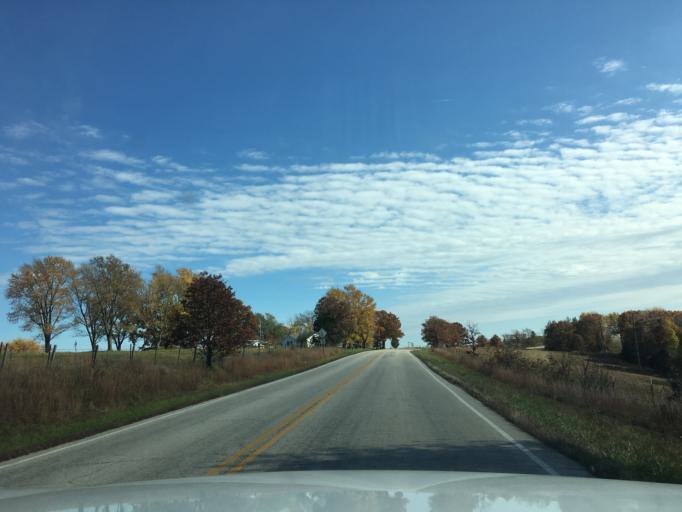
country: US
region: Missouri
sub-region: Maries County
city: Belle
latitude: 38.3240
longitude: -91.7574
